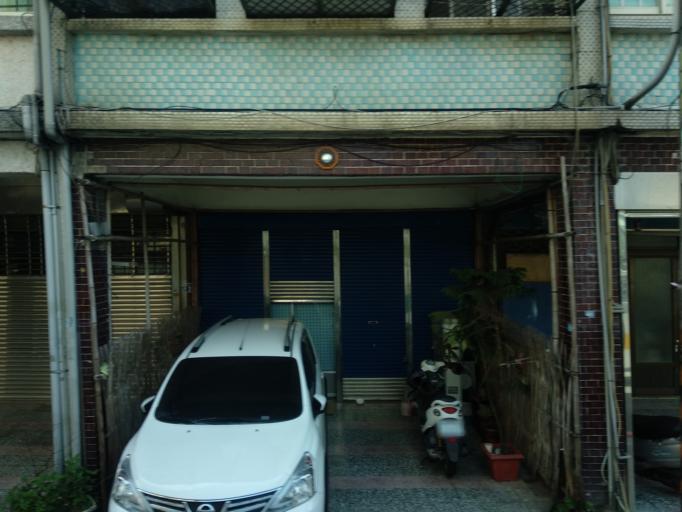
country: TW
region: Taiwan
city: Daxi
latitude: 24.7892
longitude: 121.1834
